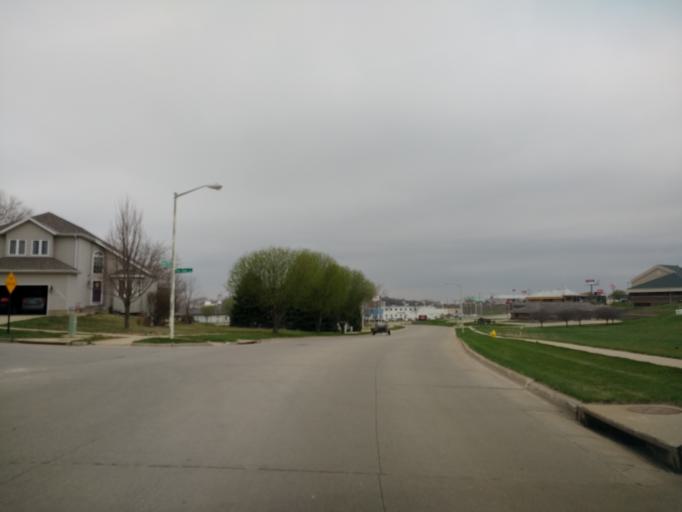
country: US
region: Iowa
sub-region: Woodbury County
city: Sergeant Bluff
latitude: 42.4365
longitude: -96.3451
